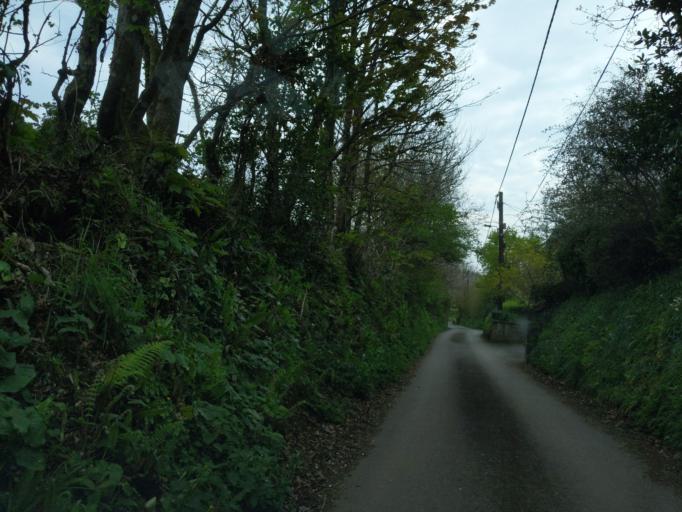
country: GB
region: England
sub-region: Devon
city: Yealmpton
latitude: 50.3518
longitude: -4.0413
